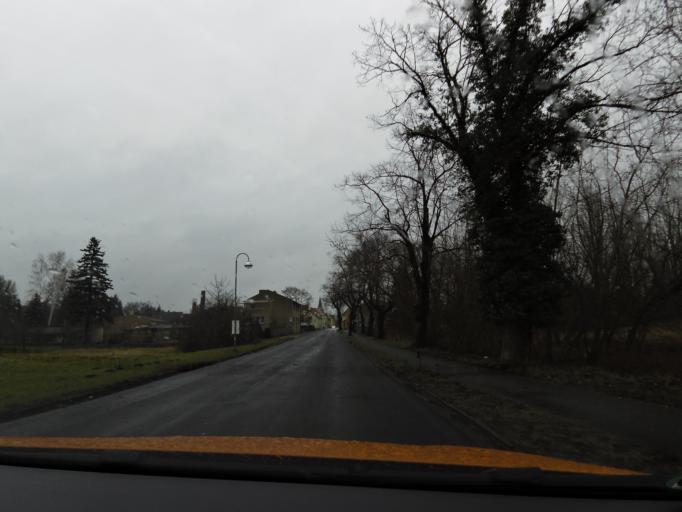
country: DE
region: Brandenburg
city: Zossen
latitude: 52.2126
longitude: 13.4443
